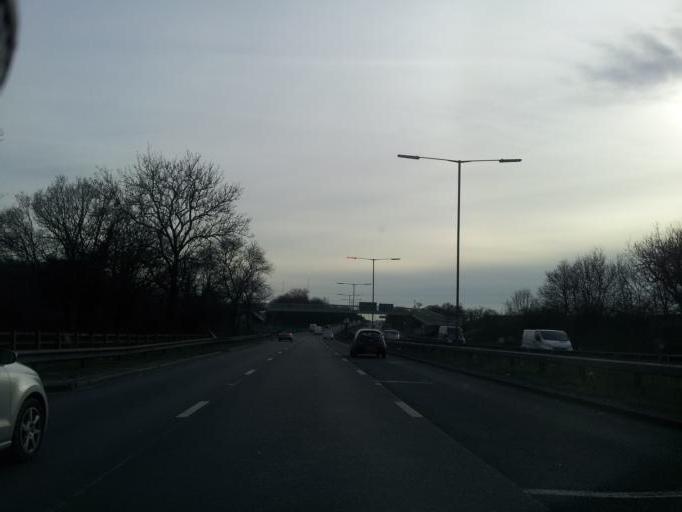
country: GB
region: England
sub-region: Greater London
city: High Barnet
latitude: 51.6739
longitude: -0.2375
